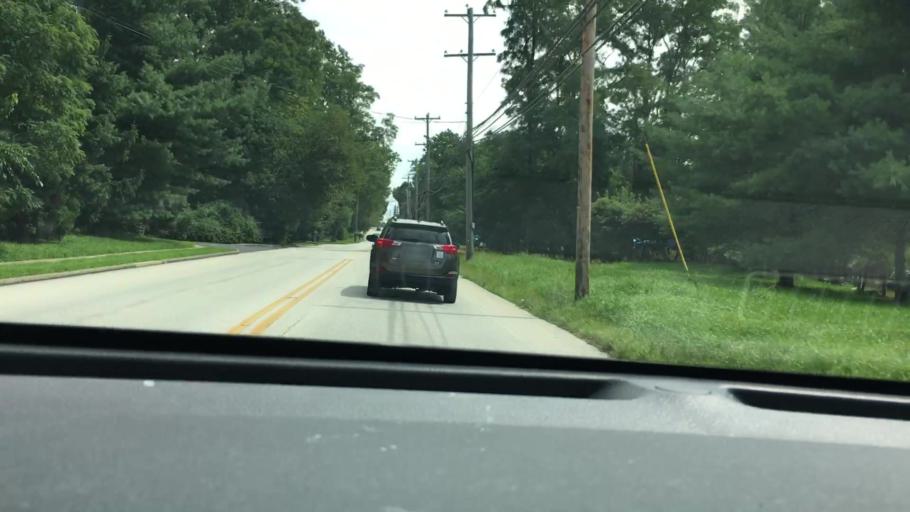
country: US
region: Pennsylvania
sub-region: Montgomery County
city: Bryn Athyn
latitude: 40.1545
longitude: -75.0673
